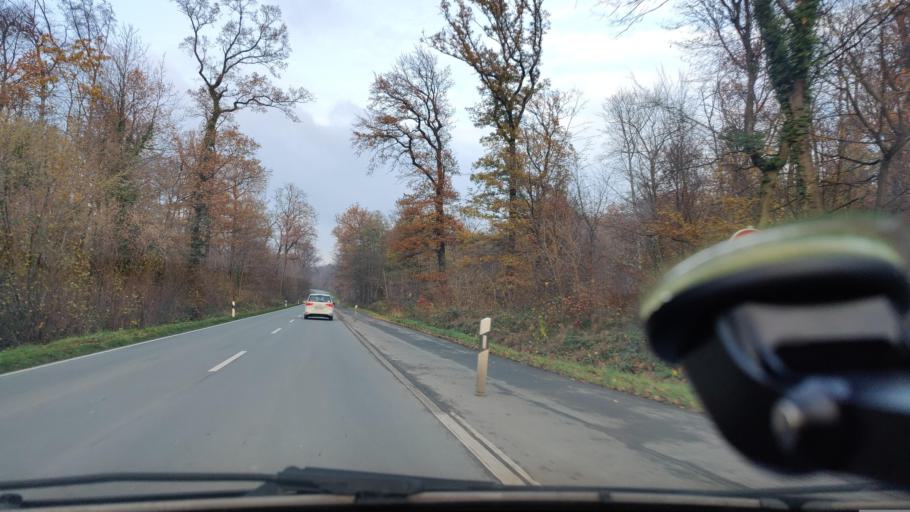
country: DE
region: North Rhine-Westphalia
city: Lunen
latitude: 51.6402
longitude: 7.5296
